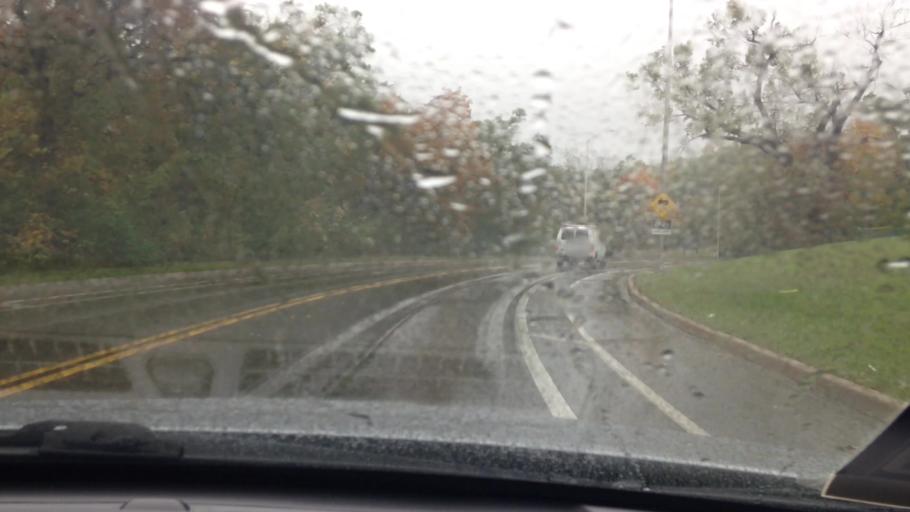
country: US
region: Missouri
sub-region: Jackson County
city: Raytown
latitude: 38.9970
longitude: -94.5339
